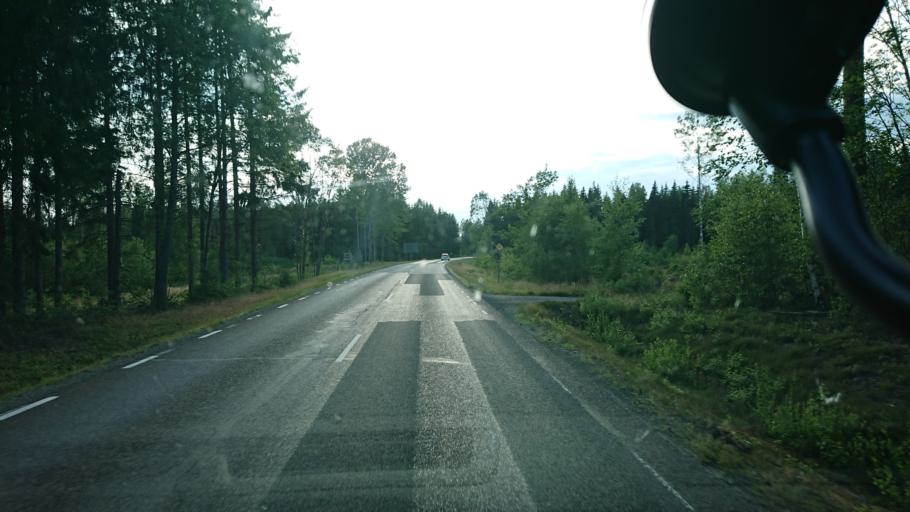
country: SE
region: Kronoberg
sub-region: Vaxjo Kommun
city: Braas
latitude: 57.0175
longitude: 15.0509
